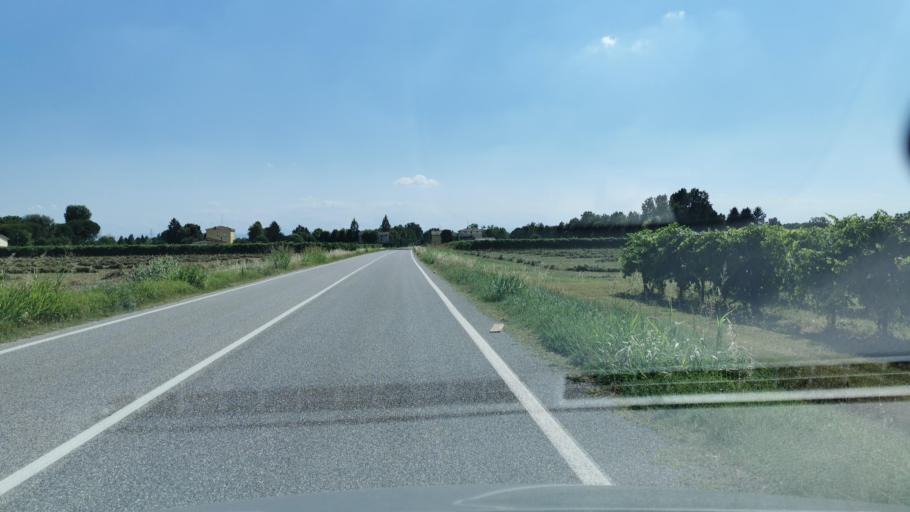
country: IT
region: Emilia-Romagna
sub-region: Provincia di Modena
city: Sam Marino
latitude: 44.7963
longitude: 10.9139
